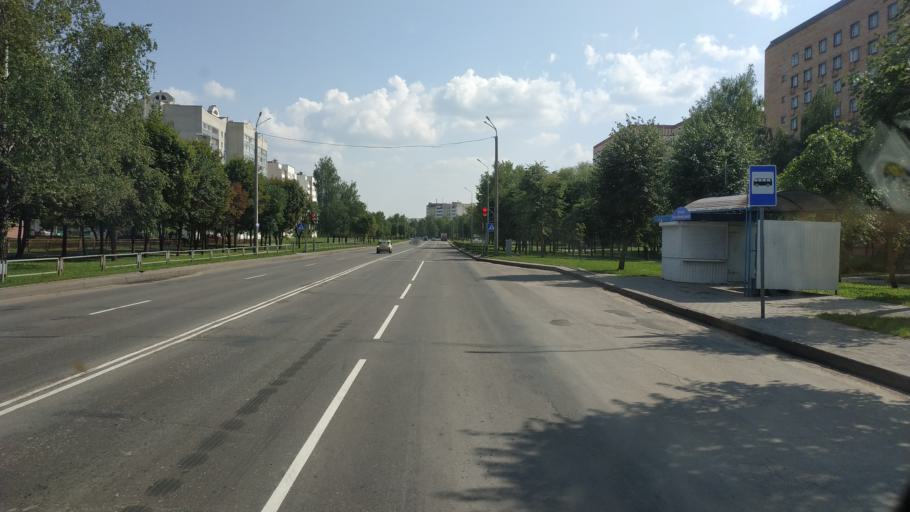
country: BY
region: Mogilev
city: Buynichy
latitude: 53.8716
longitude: 30.3130
